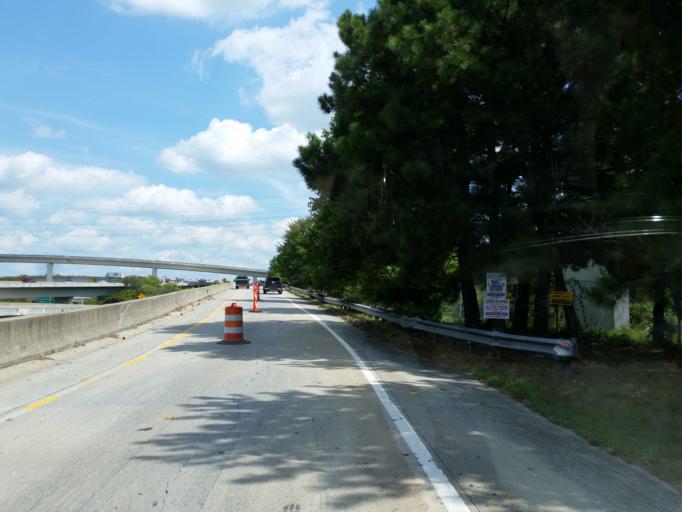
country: US
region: Georgia
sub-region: DeKalb County
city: Doraville
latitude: 33.8942
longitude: -84.2638
